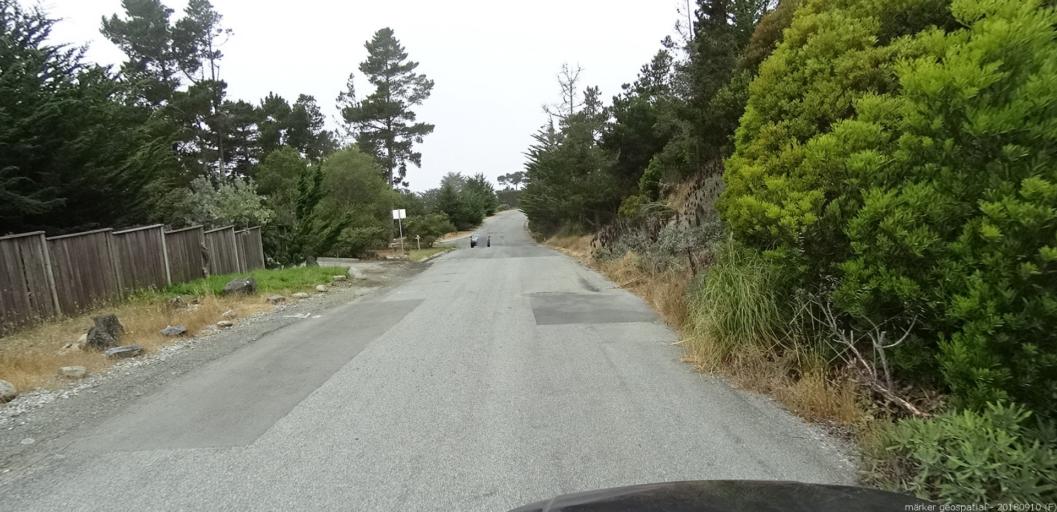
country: US
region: California
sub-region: Monterey County
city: Carmel-by-the-Sea
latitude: 36.4835
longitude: -121.9352
